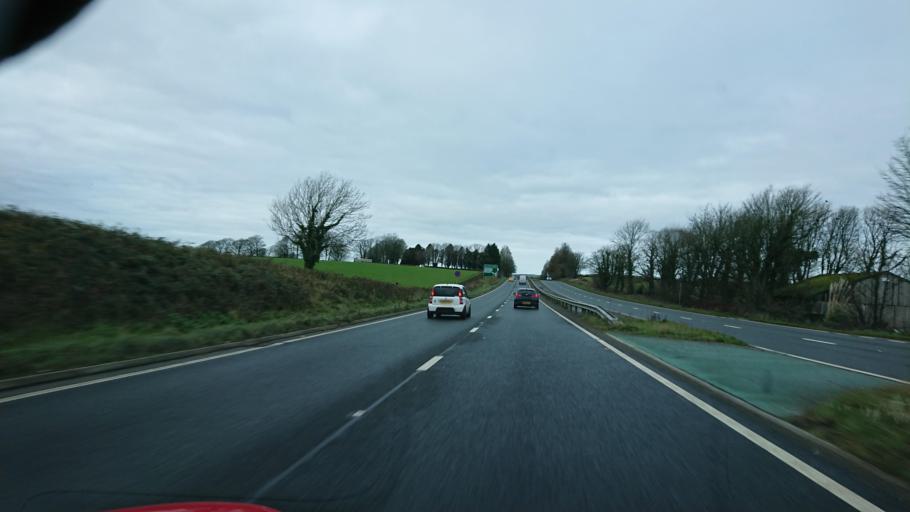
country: GB
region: England
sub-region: Cornwall
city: Liskeard
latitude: 50.4399
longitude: -4.4426
